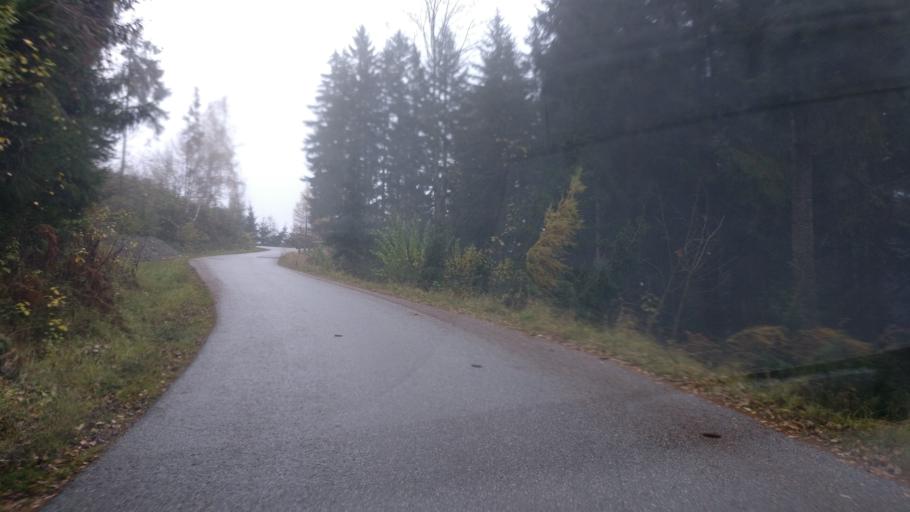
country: AT
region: Salzburg
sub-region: Politischer Bezirk Sankt Johann im Pongau
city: Filzmoos
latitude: 47.4017
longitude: 13.5272
